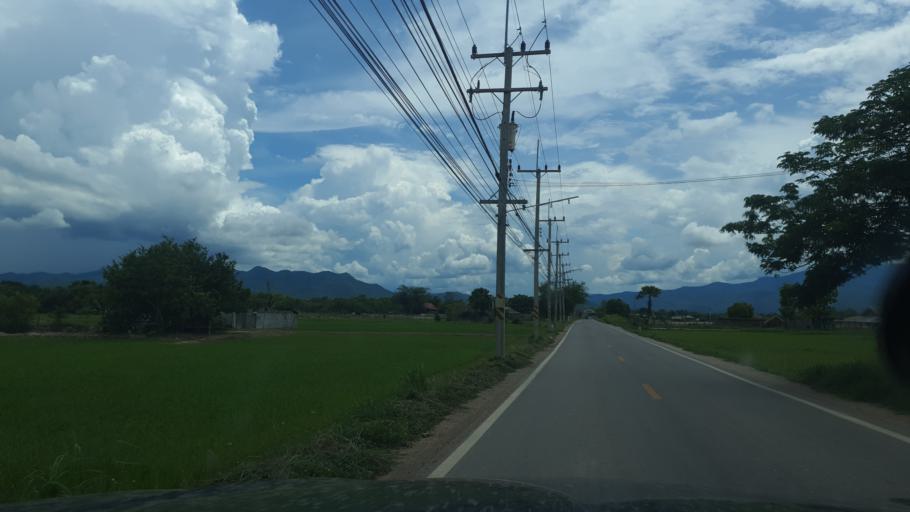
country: TH
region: Lampang
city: Sop Prap
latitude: 17.8804
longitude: 99.3726
